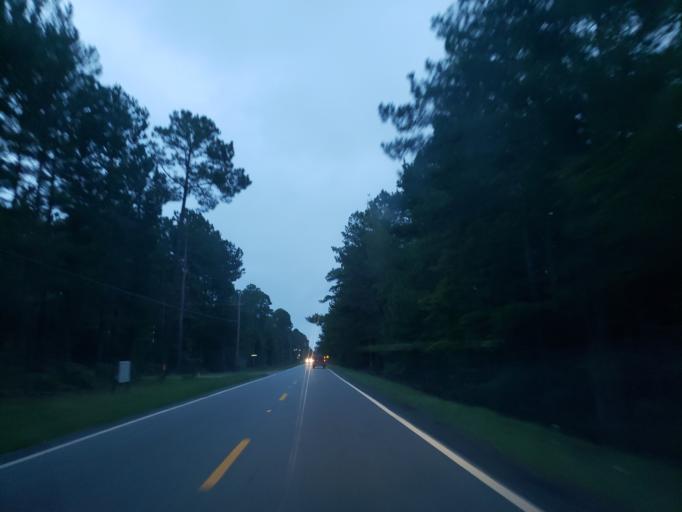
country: US
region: Georgia
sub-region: Chatham County
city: Bloomingdale
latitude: 32.0905
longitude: -81.3469
